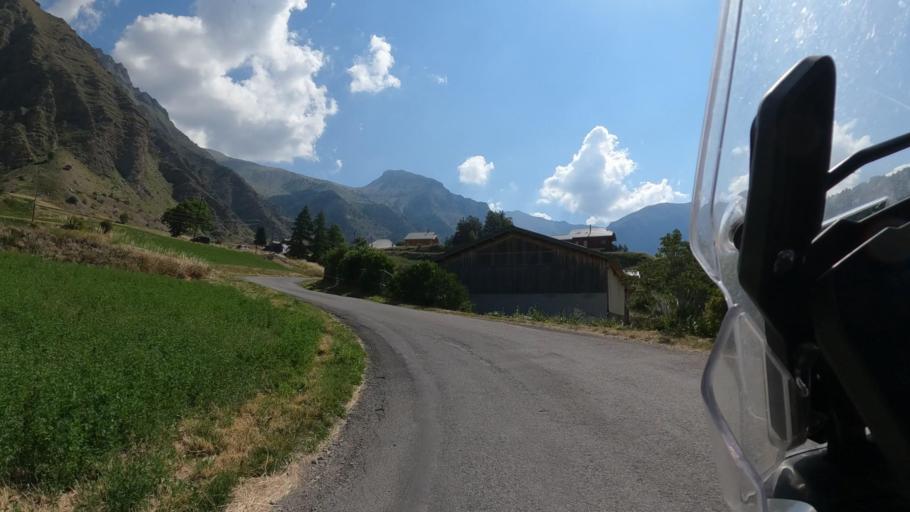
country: FR
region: Provence-Alpes-Cote d'Azur
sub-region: Departement des Hautes-Alpes
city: Guillestre
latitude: 44.5463
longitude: 6.6162
